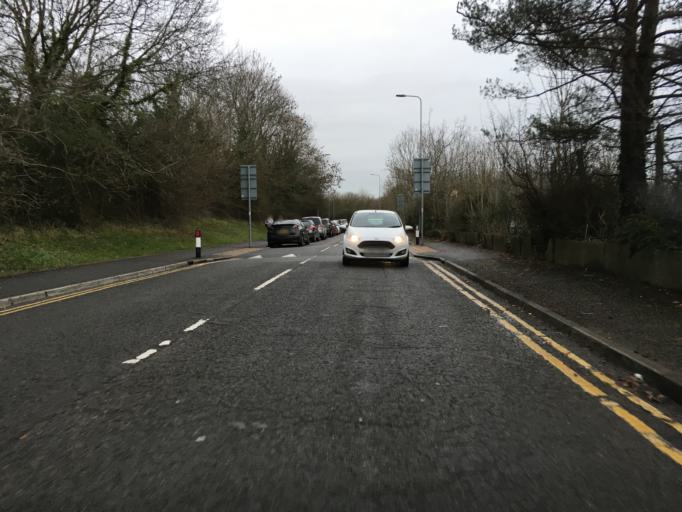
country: GB
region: Wales
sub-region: Cardiff
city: Cardiff
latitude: 51.5096
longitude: -3.1465
